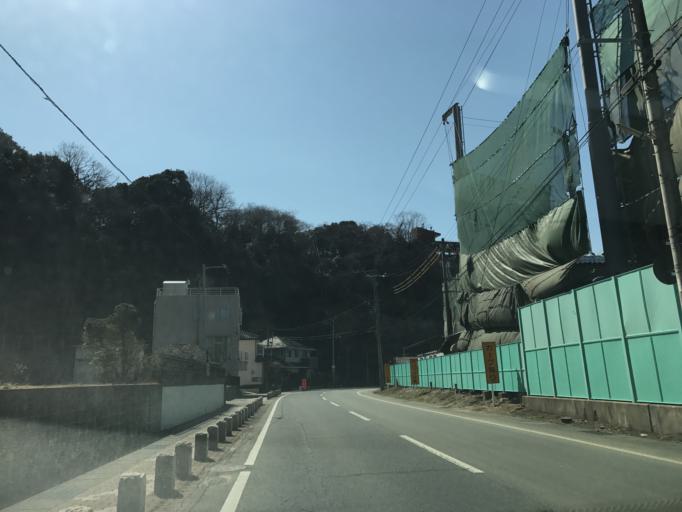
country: JP
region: Fukushima
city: Iwaki
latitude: 36.9396
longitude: 140.9166
